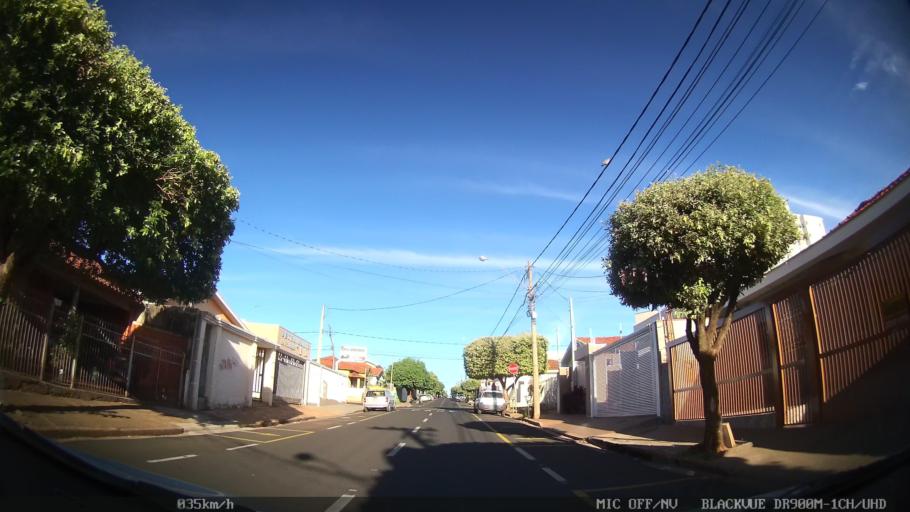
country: BR
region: Sao Paulo
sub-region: Sao Jose Do Rio Preto
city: Sao Jose do Rio Preto
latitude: -20.8260
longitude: -49.3790
